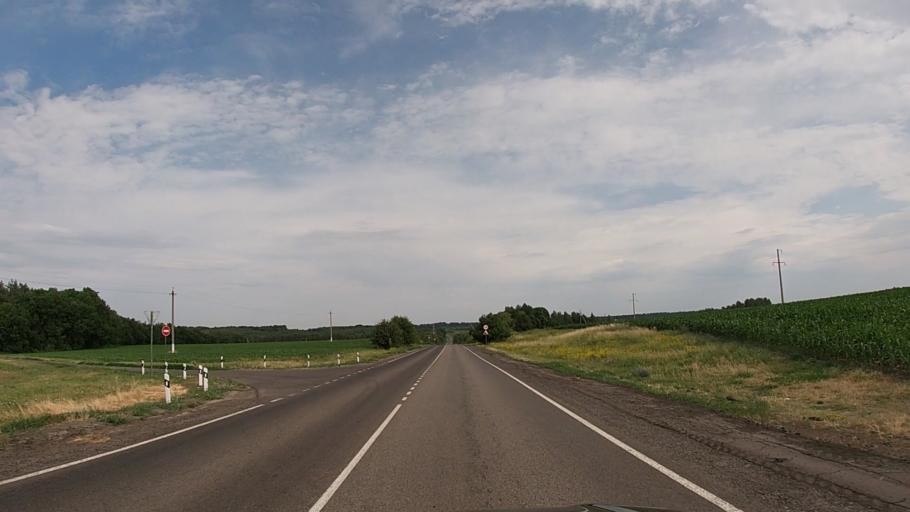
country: RU
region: Belgorod
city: Krasnaya Yaruga
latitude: 50.8219
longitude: 35.5012
